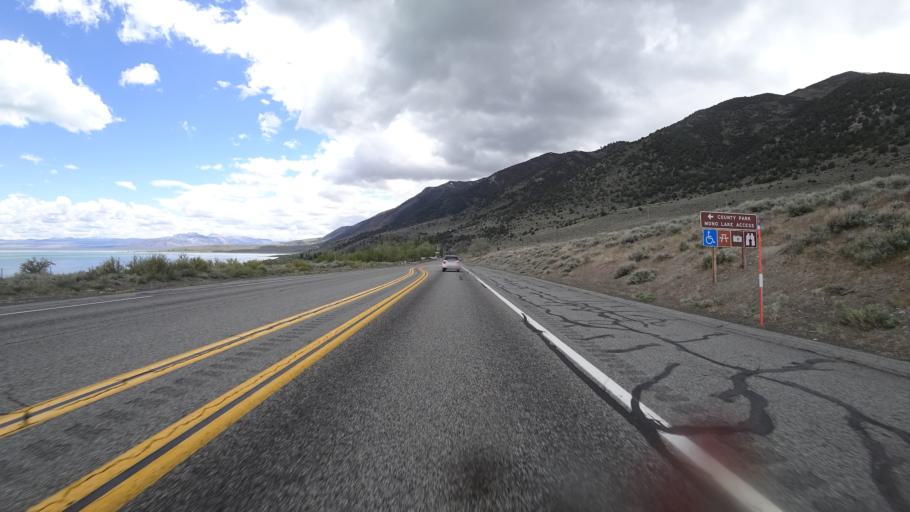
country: US
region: California
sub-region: Mono County
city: Bridgeport
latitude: 38.0124
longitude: -119.1550
